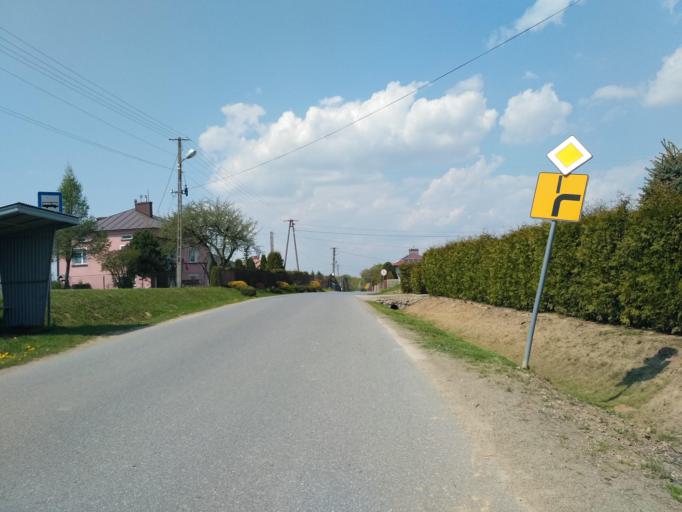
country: PL
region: Subcarpathian Voivodeship
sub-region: Powiat jasielski
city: Debowiec
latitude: 49.6973
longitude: 21.5079
